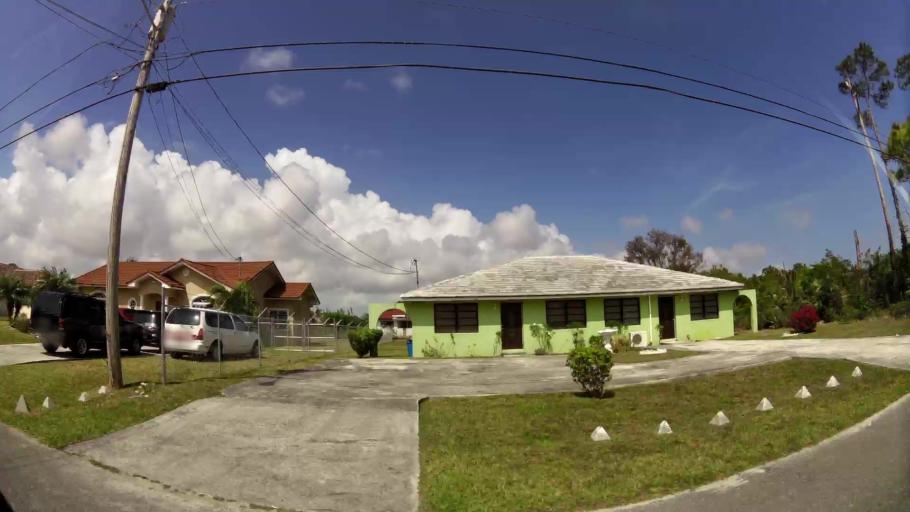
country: BS
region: Freeport
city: Freeport
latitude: 26.5018
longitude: -78.7042
